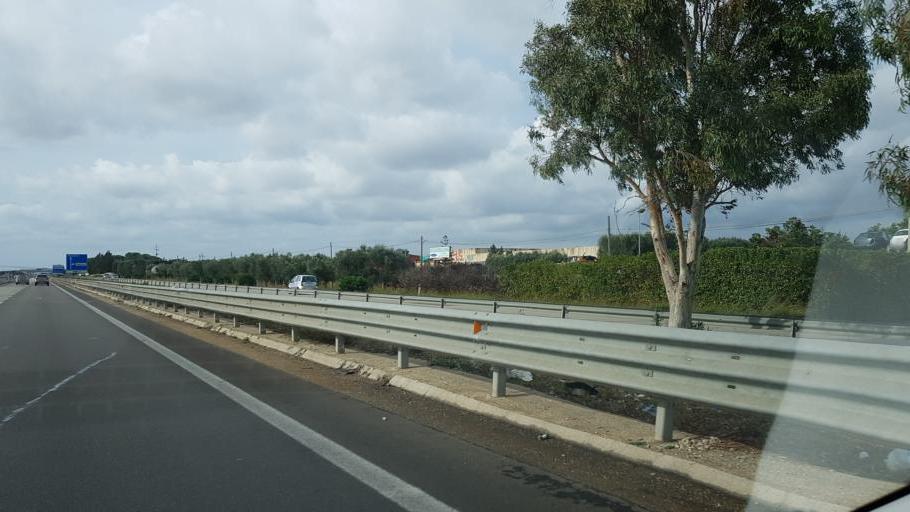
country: IT
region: Apulia
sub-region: Provincia di Brindisi
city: Brindisi
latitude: 40.6098
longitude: 17.8917
